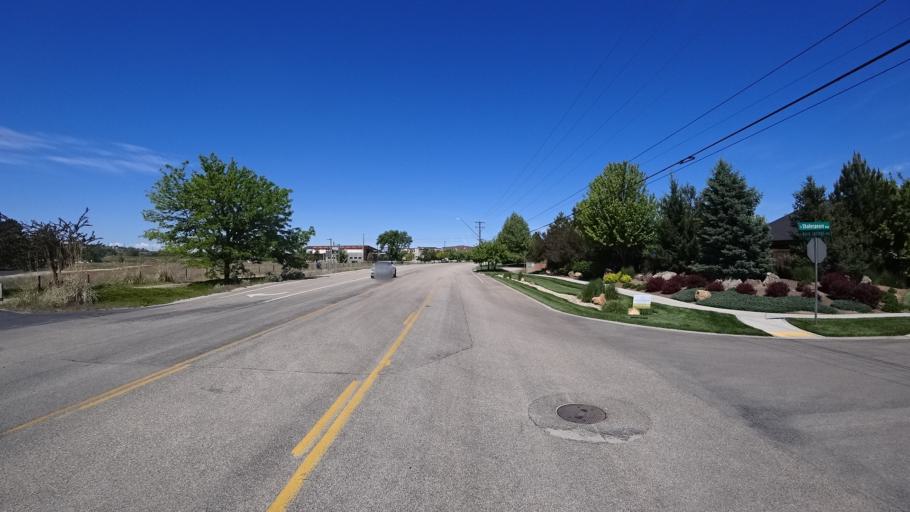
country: US
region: Idaho
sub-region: Ada County
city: Boise
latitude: 43.5644
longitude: -116.1121
